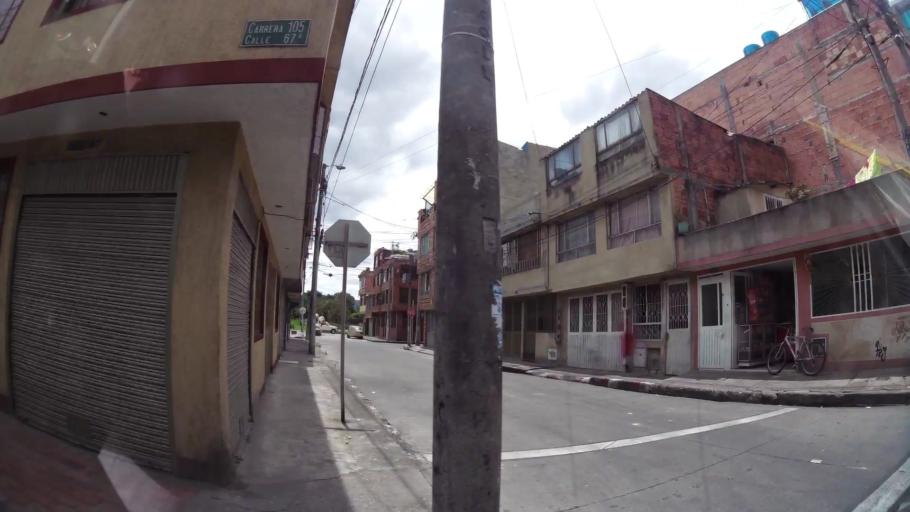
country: CO
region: Cundinamarca
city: Funza
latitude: 4.6989
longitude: -74.1236
